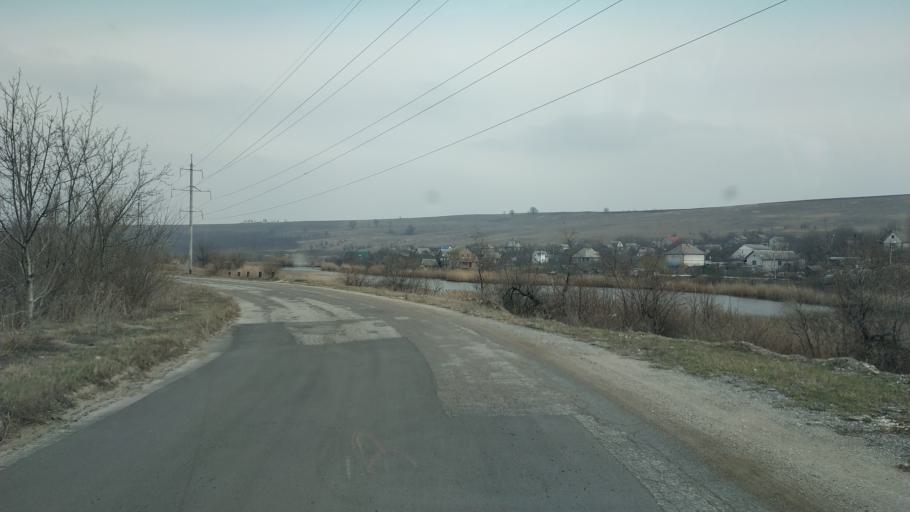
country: MD
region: Chisinau
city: Singera
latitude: 46.8928
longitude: 29.0151
